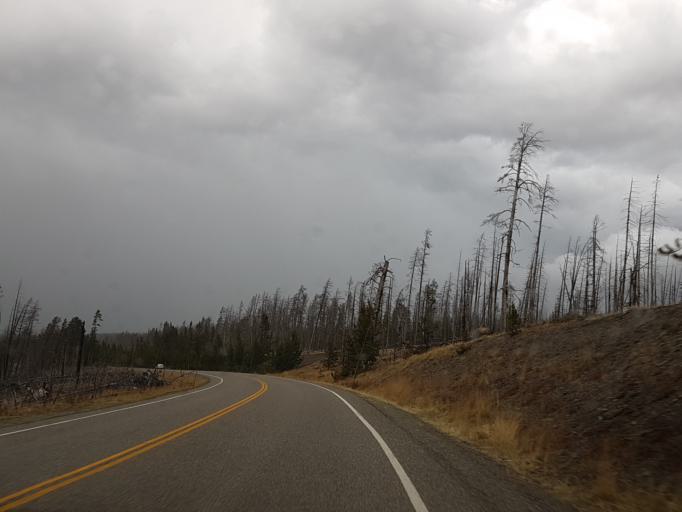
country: US
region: Montana
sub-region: Gallatin County
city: West Yellowstone
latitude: 44.4689
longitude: -110.5179
